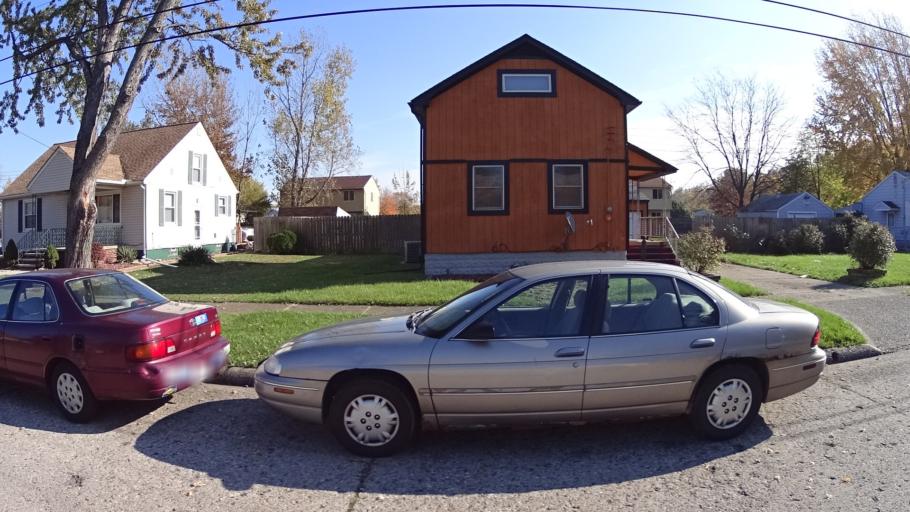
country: US
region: Ohio
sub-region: Lorain County
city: Lorain
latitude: 41.4677
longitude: -82.1537
